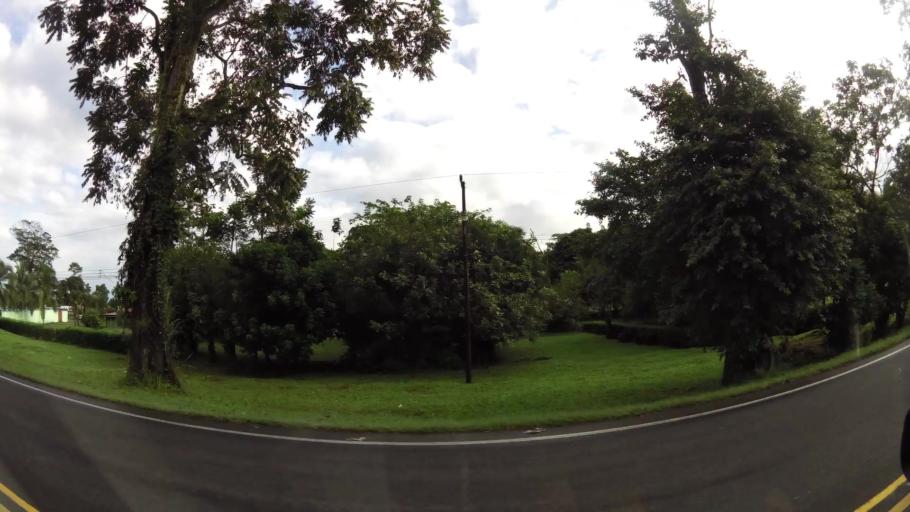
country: CR
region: Limon
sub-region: Canton de Pococi
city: Guapiles
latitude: 10.2095
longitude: -83.8343
